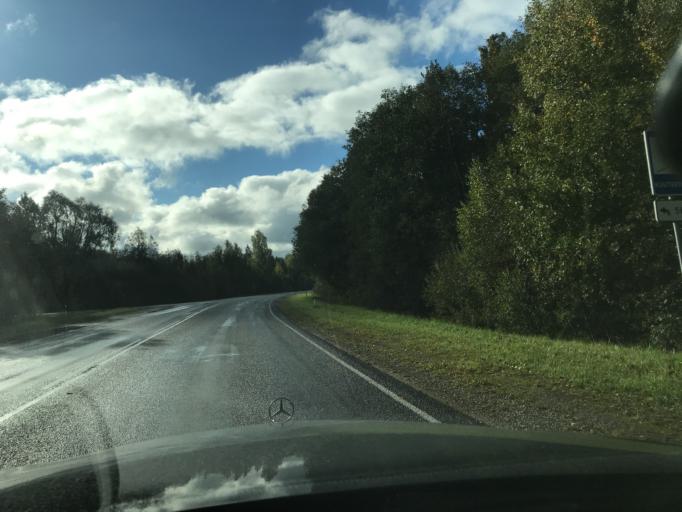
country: EE
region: Tartu
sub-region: Elva linn
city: Elva
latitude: 58.0000
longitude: 26.2682
